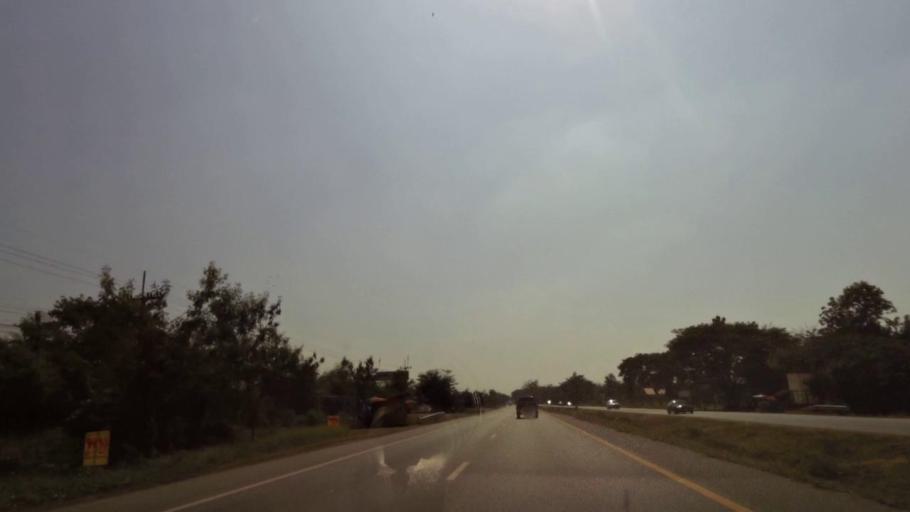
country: TH
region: Phichit
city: Bueng Na Rang
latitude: 16.3440
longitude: 100.1282
